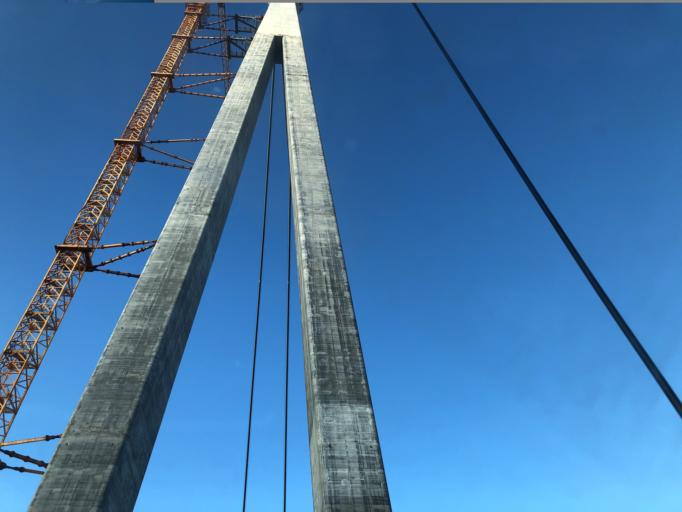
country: NO
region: Nordland
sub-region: Narvik
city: Narvik
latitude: 68.4643
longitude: 17.4819
